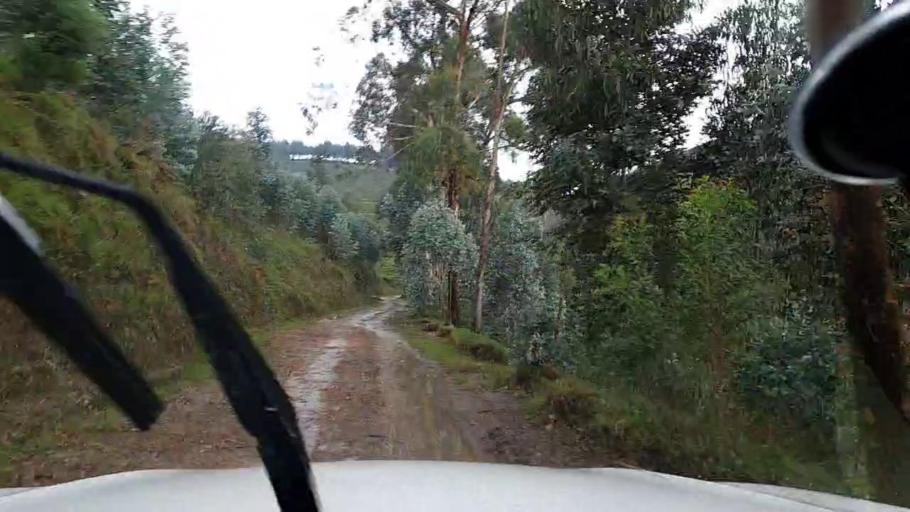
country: RW
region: Western Province
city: Kibuye
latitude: -2.0791
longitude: 29.5147
